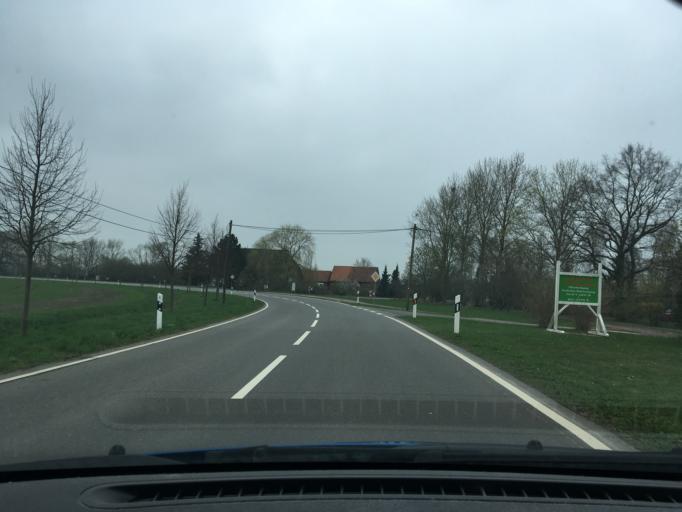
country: DE
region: Lower Saxony
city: Neu Darchau
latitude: 53.3111
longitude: 10.8914
